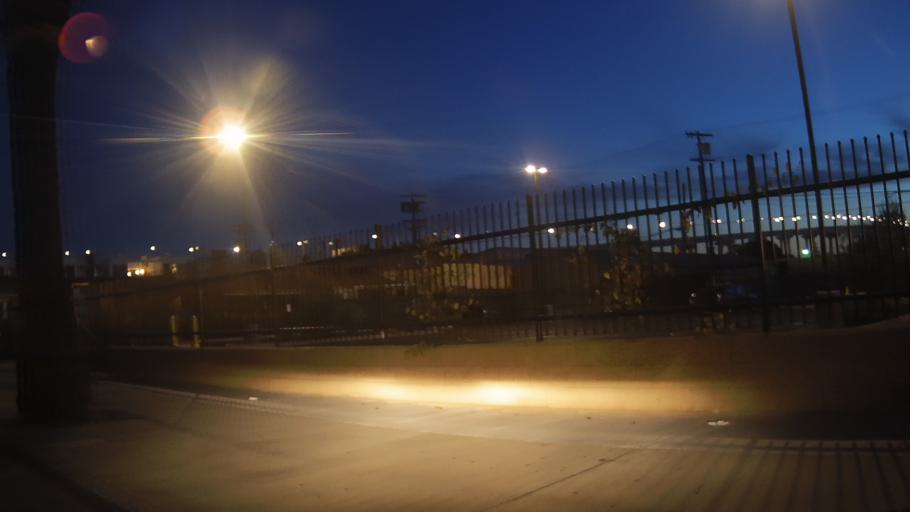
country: US
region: California
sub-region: San Diego County
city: San Diego
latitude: 32.7014
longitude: -117.1463
